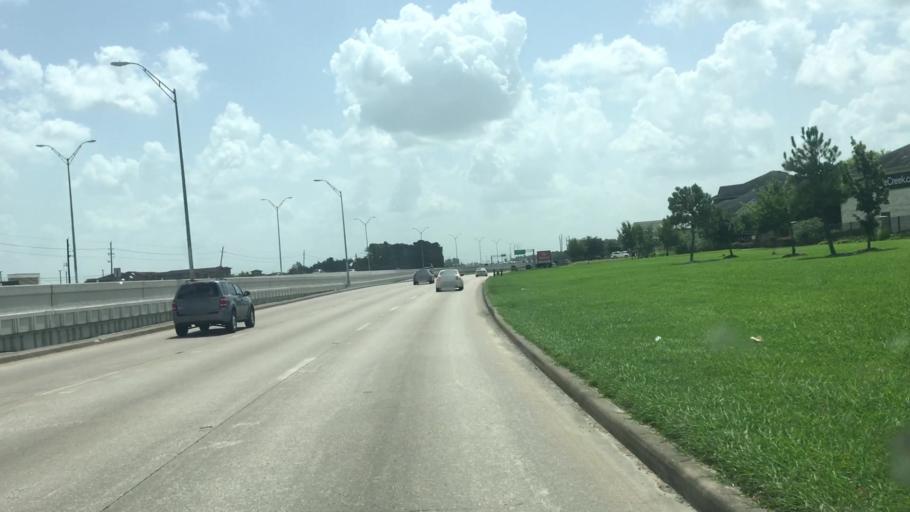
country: US
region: Texas
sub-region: Harris County
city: Humble
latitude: 29.9342
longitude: -95.2442
